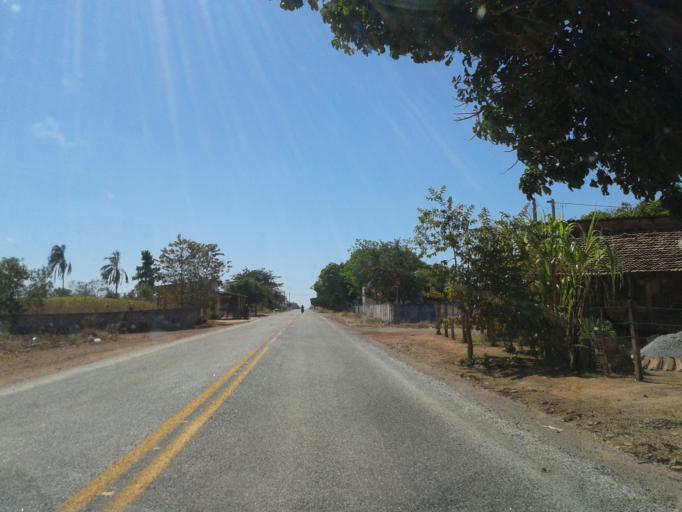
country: BR
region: Goias
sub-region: Sao Miguel Do Araguaia
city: Sao Miguel do Araguaia
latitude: -13.2637
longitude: -50.1489
